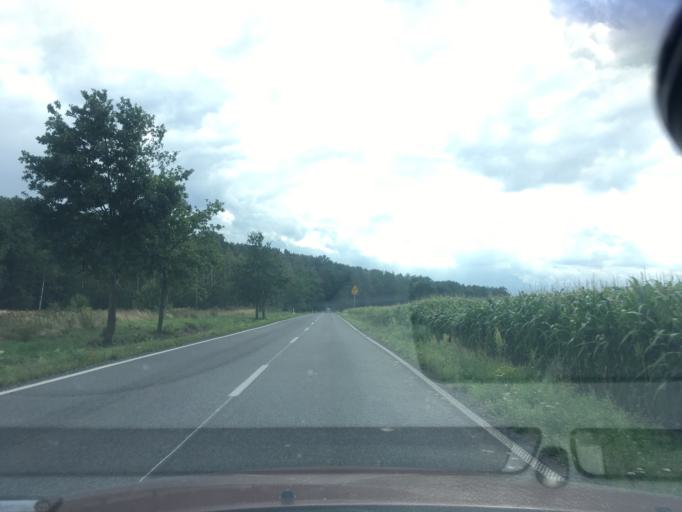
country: PL
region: Lower Silesian Voivodeship
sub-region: Powiat zgorzelecki
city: Piensk
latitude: 51.2225
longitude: 15.0257
